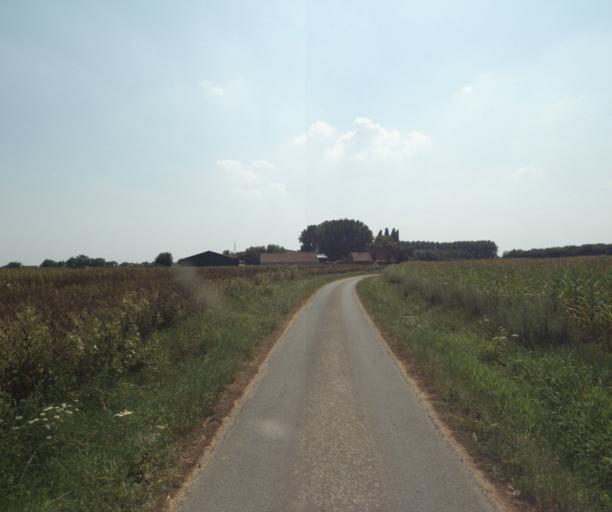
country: FR
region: Nord-Pas-de-Calais
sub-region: Departement du Nord
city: Wambrechies
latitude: 50.7110
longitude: 3.0438
